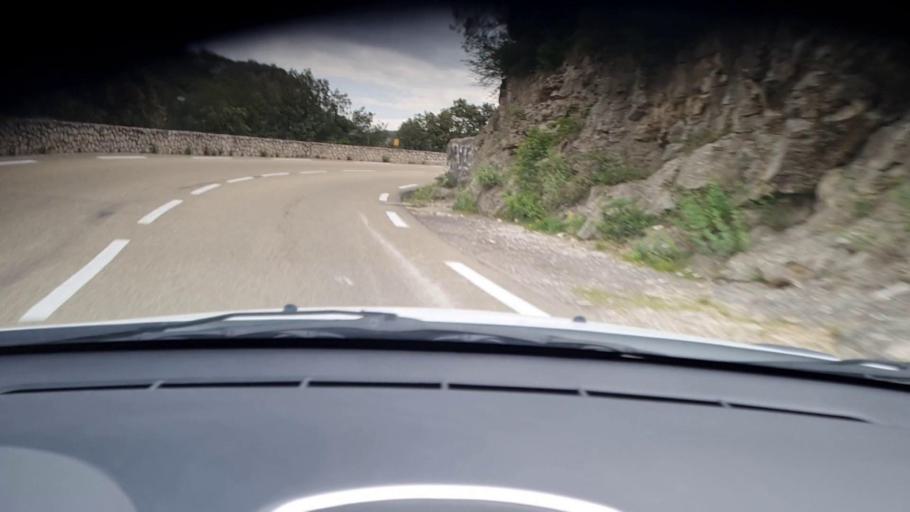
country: FR
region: Languedoc-Roussillon
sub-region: Departement du Gard
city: Blauzac
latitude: 43.9346
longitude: 4.3849
